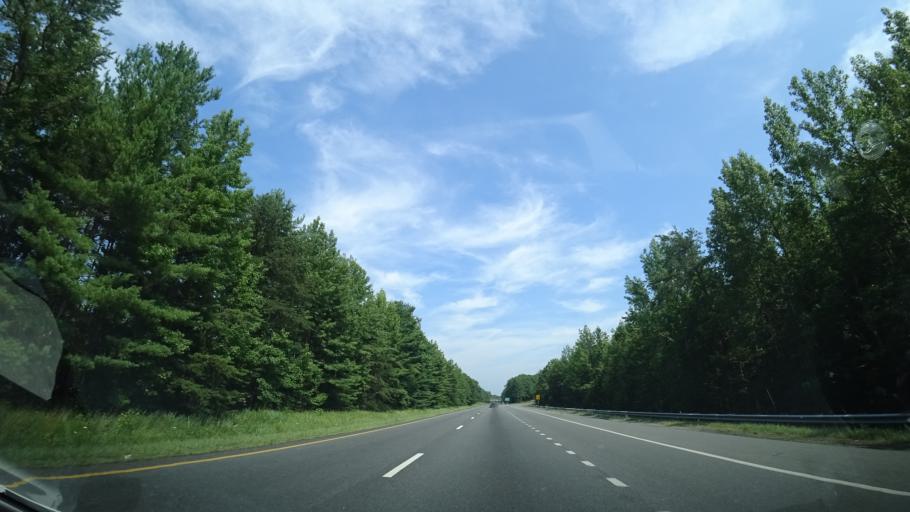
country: US
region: Virginia
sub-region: Louisa County
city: Louisa
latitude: 37.9426
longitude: -78.1149
